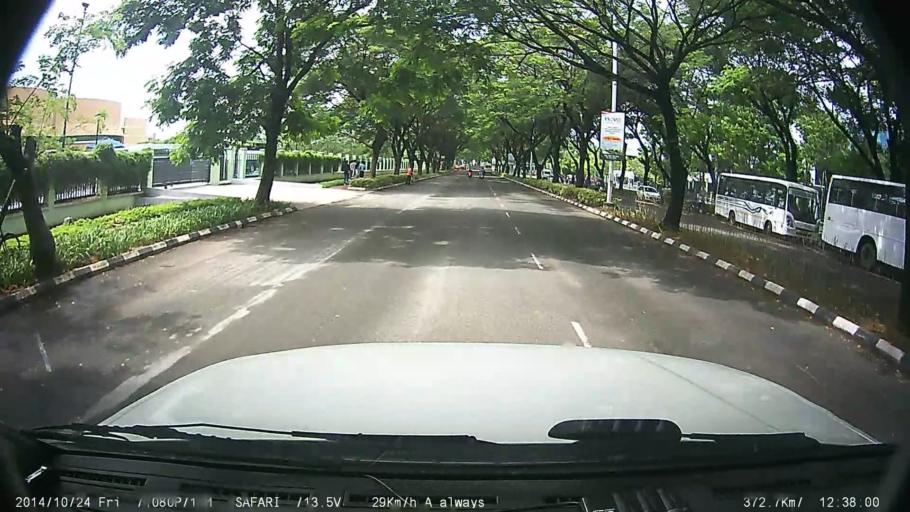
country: IN
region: Tamil Nadu
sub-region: Kancheepuram
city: Singapperumalkovil
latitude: 12.7368
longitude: 80.0053
